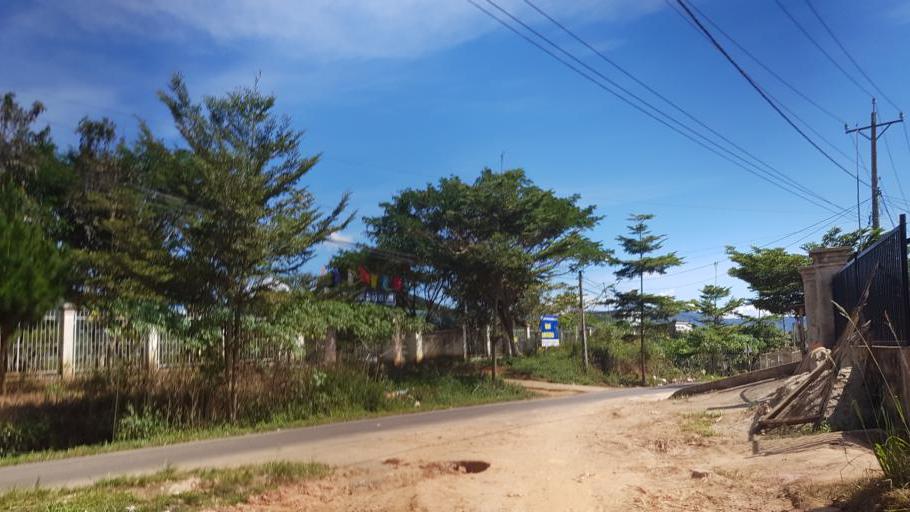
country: VN
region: Lam Dong
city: Da Lat
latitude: 11.8792
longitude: 108.3421
